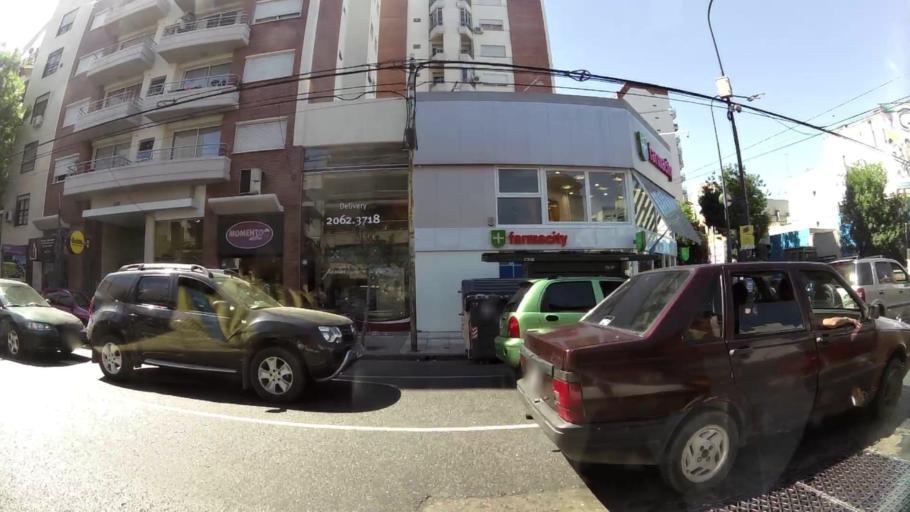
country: AR
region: Buenos Aires F.D.
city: Buenos Aires
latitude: -34.6238
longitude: -58.4023
